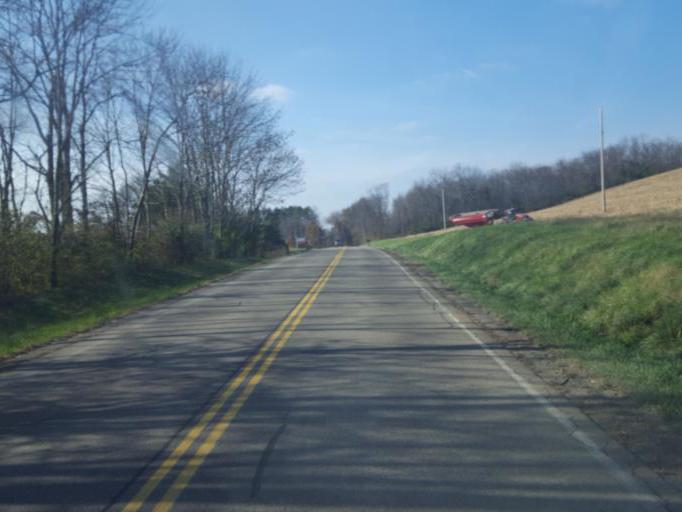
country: US
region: Ohio
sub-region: Knox County
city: Oak Hill
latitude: 40.3896
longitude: -82.2612
